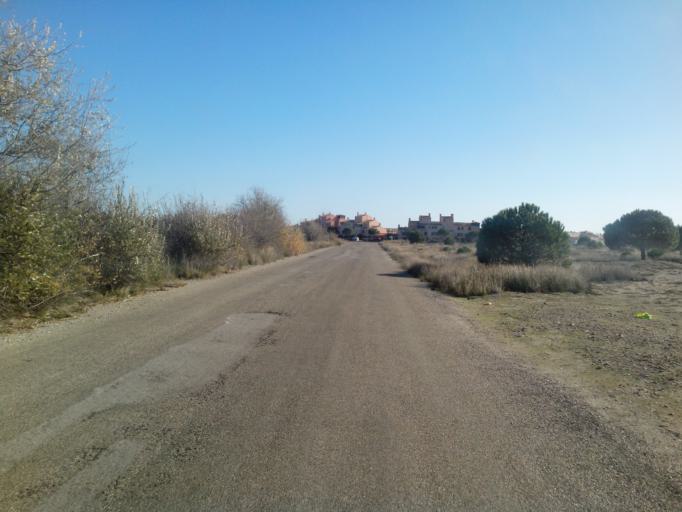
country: FR
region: Languedoc-Roussillon
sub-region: Departement des Pyrenees-Orientales
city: Le Barcares
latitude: 42.8399
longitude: 3.0303
